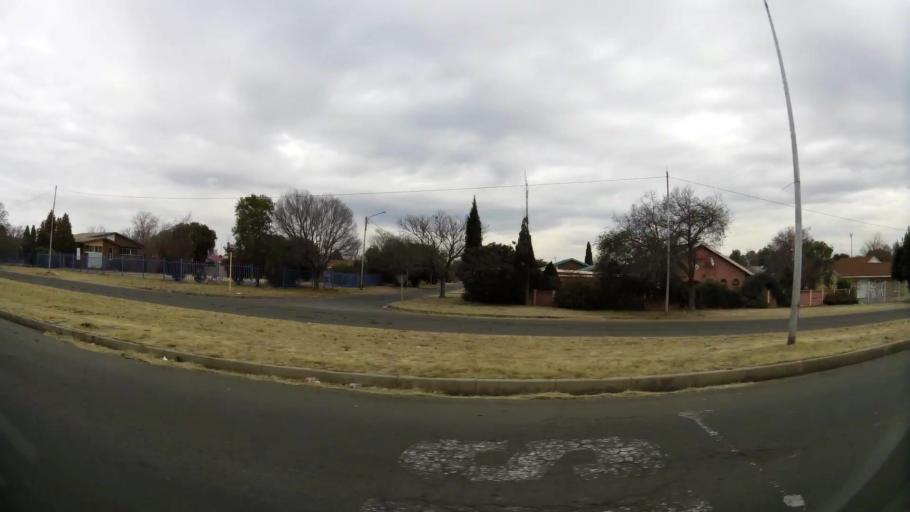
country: ZA
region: Orange Free State
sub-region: Fezile Dabi District Municipality
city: Kroonstad
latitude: -27.6419
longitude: 27.2331
